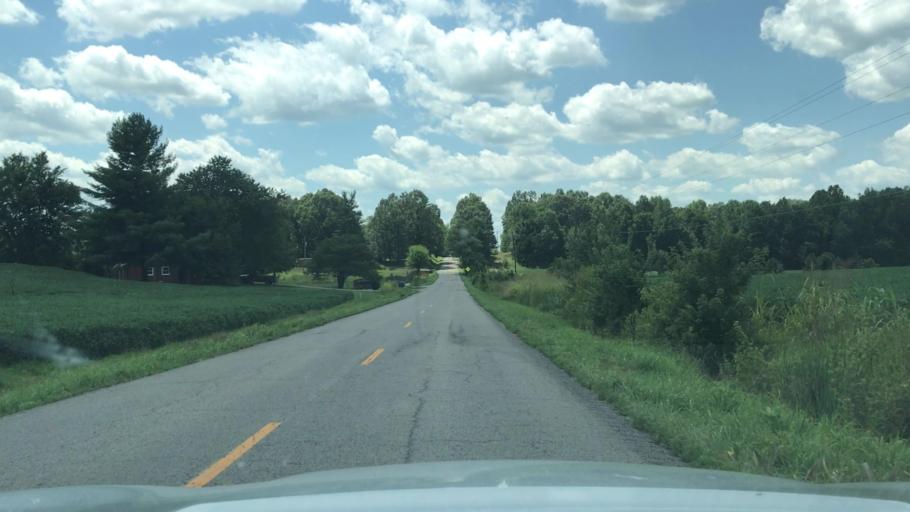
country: US
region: Kentucky
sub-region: Muhlenberg County
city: Greenville
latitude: 37.1348
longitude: -87.2727
